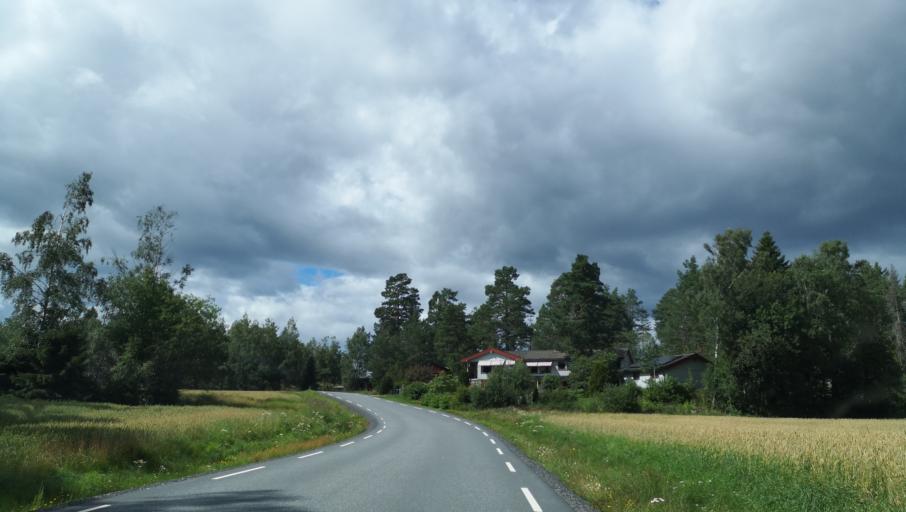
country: NO
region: Ostfold
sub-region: Hobol
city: Tomter
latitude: 59.6732
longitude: 10.9745
